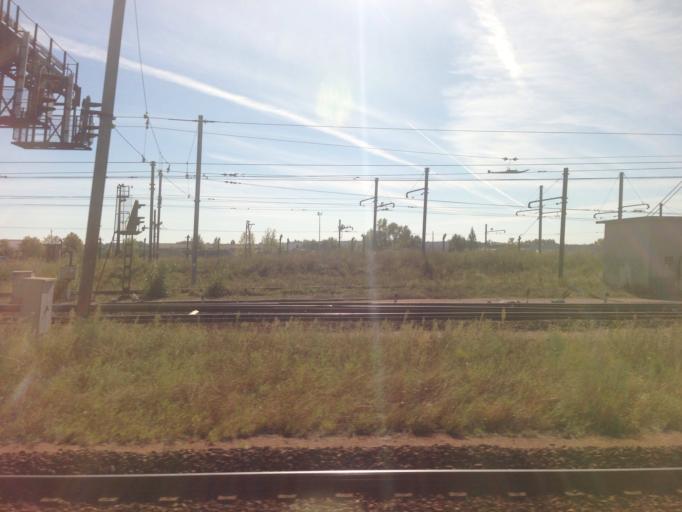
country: FR
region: Centre
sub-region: Departement d'Indre-et-Loire
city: La Ville-aux-Dames
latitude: 47.3924
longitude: 0.7628
